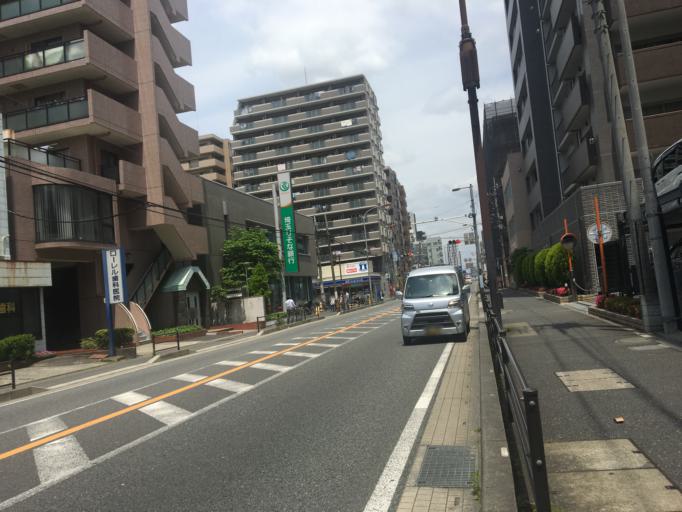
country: JP
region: Saitama
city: Shimotoda
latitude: 35.8096
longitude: 139.6829
